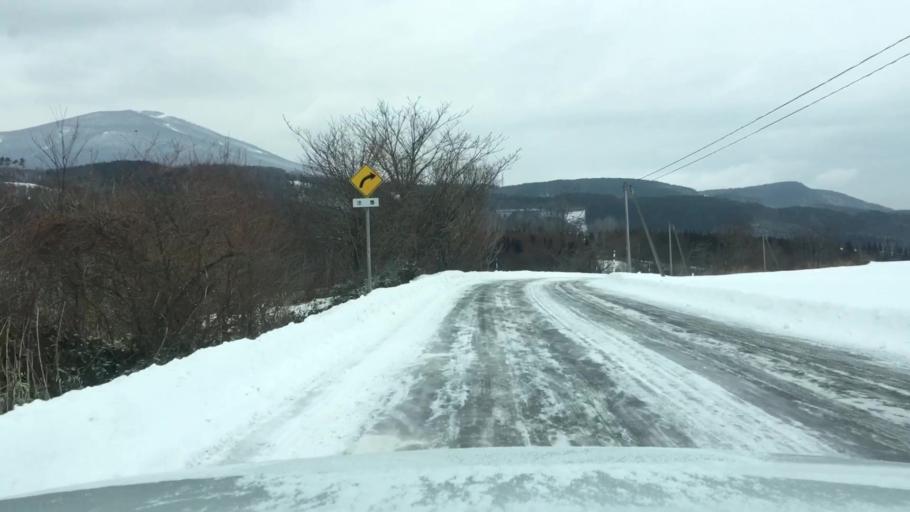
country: JP
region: Iwate
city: Shizukuishi
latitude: 39.9341
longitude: 141.0017
